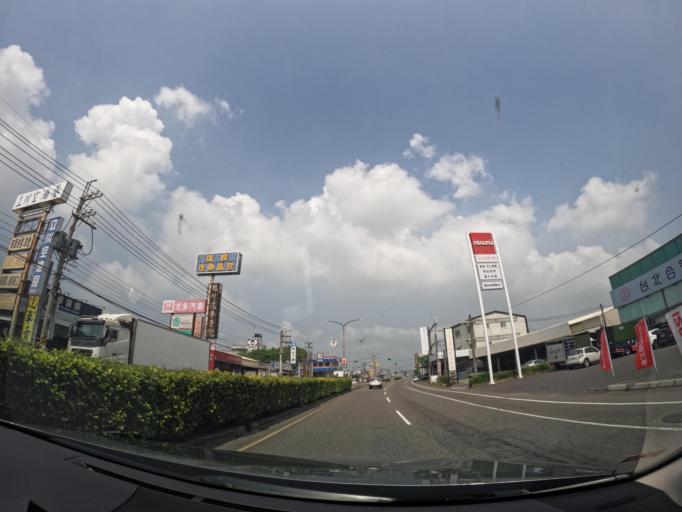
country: TW
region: Taiwan
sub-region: Yunlin
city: Douliu
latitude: 23.6964
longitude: 120.4614
